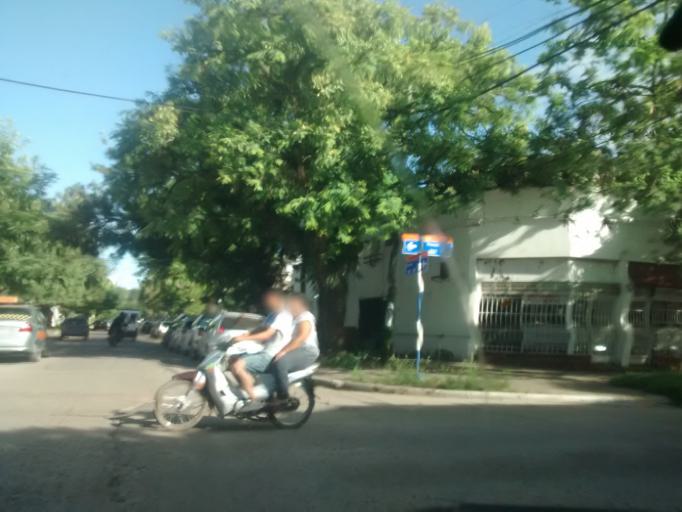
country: AR
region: Chaco
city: Resistencia
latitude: -27.4495
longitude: -58.9778
